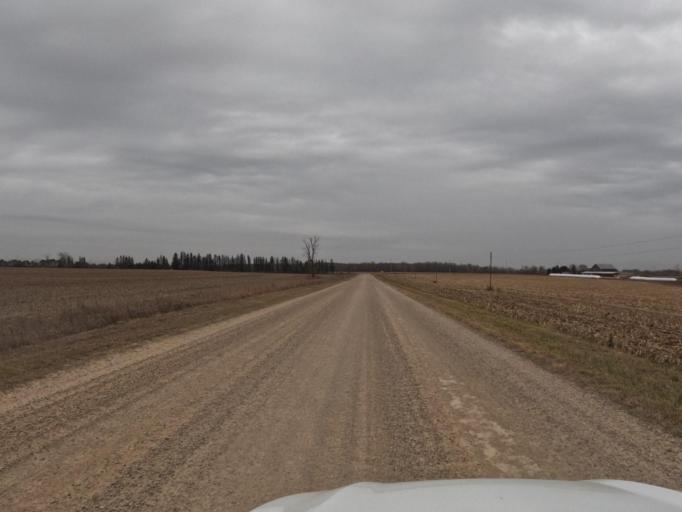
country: CA
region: Ontario
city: Shelburne
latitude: 43.8699
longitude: -80.3555
